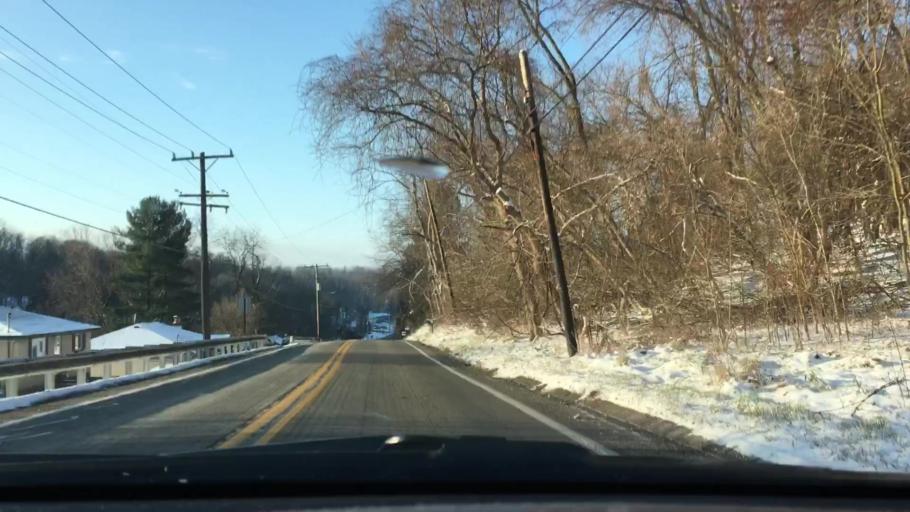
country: US
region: Pennsylvania
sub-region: Allegheny County
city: Clairton
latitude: 40.2698
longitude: -79.8478
